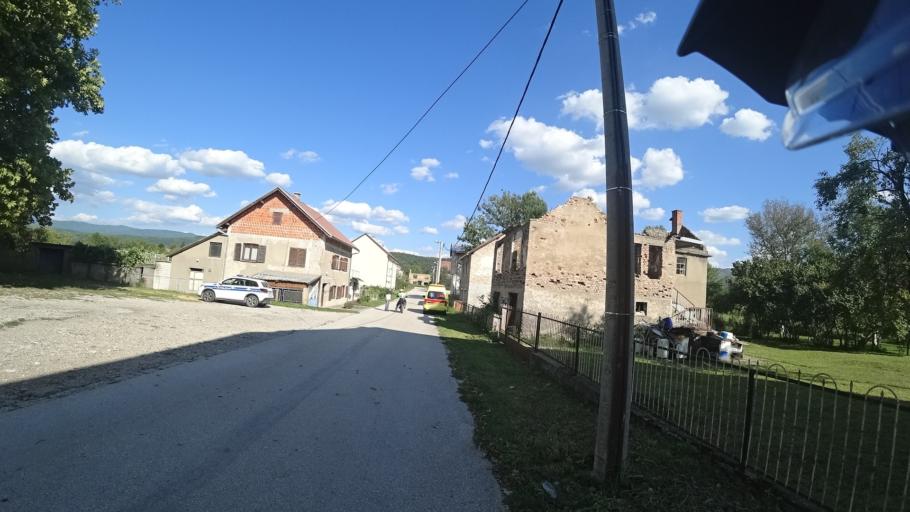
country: BA
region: Federation of Bosnia and Herzegovina
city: Orasac
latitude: 44.3636
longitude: 16.1245
